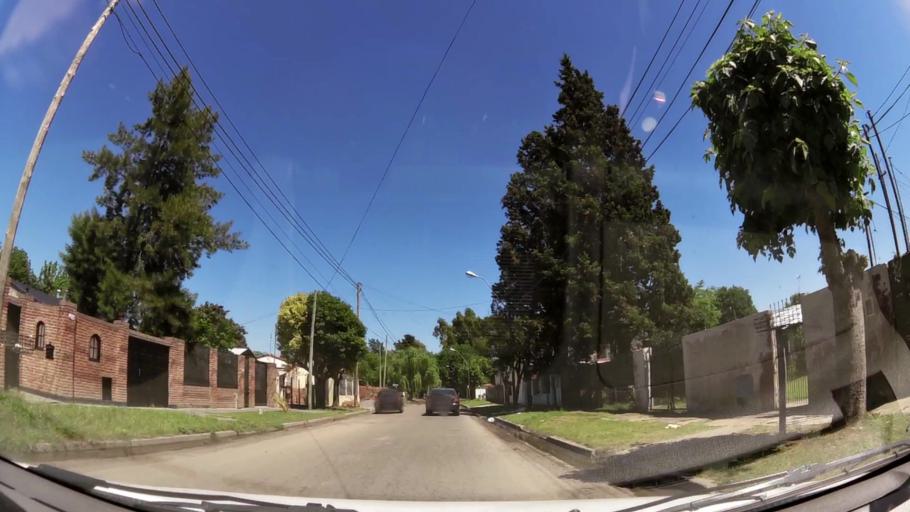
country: AR
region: Buenos Aires
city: Ituzaingo
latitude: -34.6815
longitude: -58.6558
